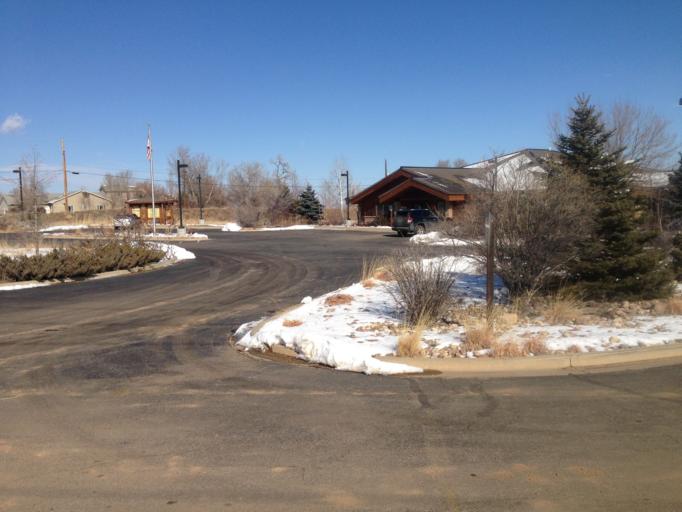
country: US
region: Colorado
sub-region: Boulder County
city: Boulder
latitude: 40.0575
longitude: -105.2692
